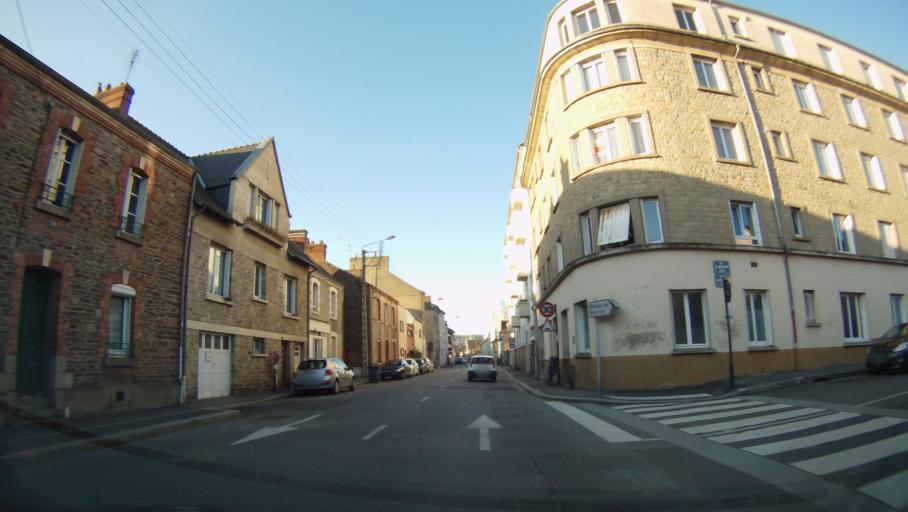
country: FR
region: Brittany
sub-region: Departement d'Ille-et-Vilaine
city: Rennes
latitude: 48.0982
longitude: -1.6720
